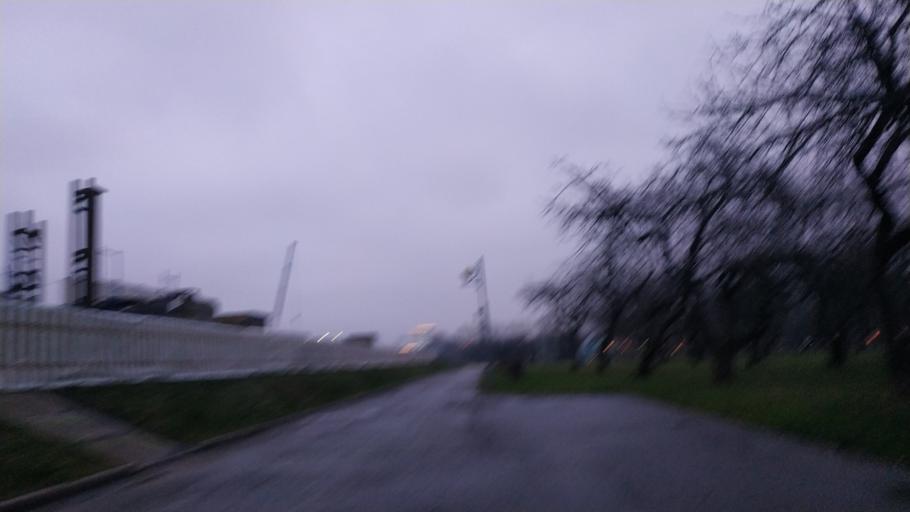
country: RU
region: Moskovskaya
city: Levoberezhnyy
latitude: 55.8527
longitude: 37.4411
